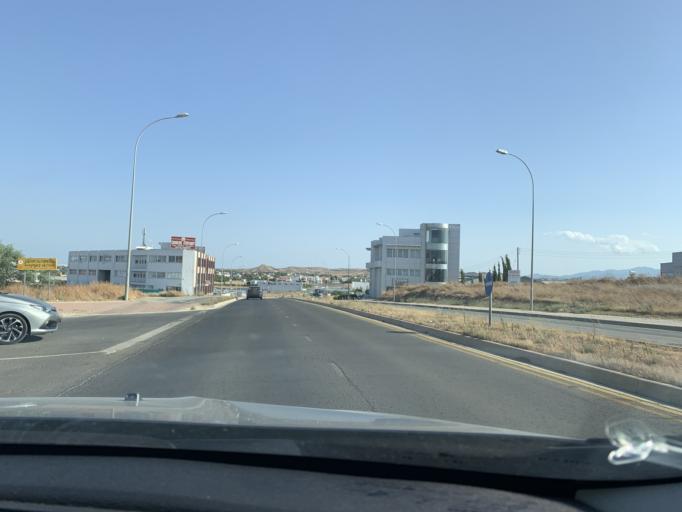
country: CY
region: Lefkosia
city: Nicosia
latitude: 35.1217
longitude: 33.3563
